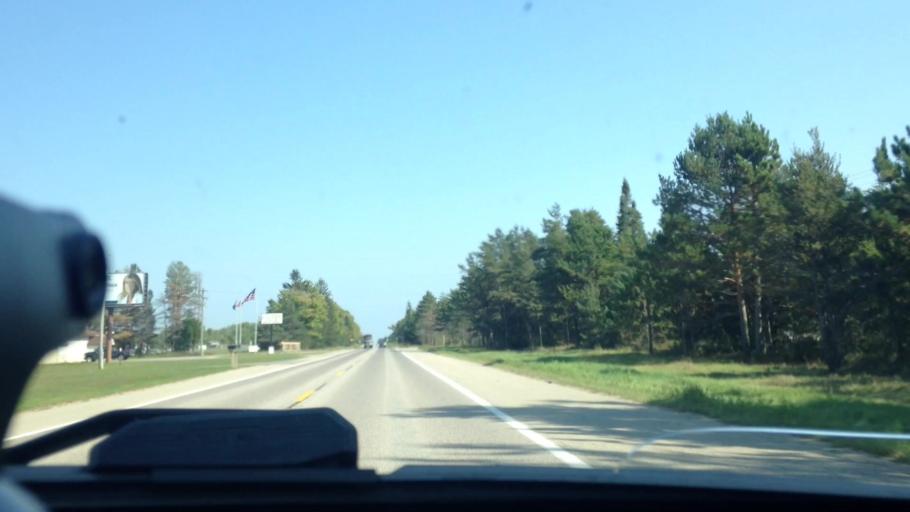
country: US
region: Michigan
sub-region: Luce County
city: Newberry
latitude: 46.3034
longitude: -85.4702
